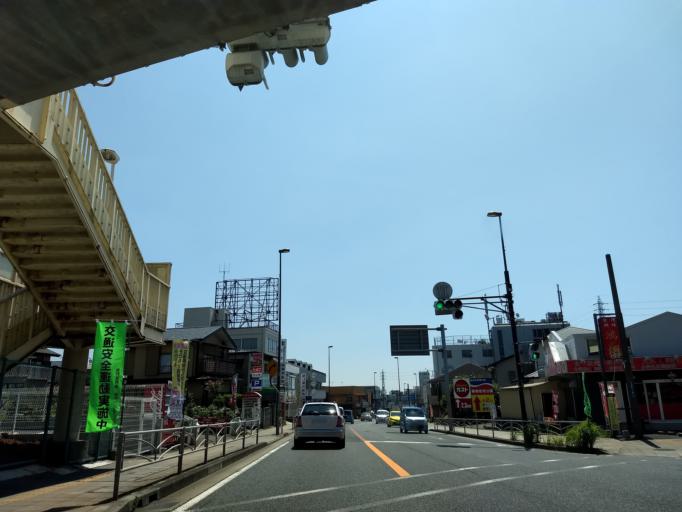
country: JP
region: Kanagawa
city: Hadano
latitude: 35.3770
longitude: 139.1813
